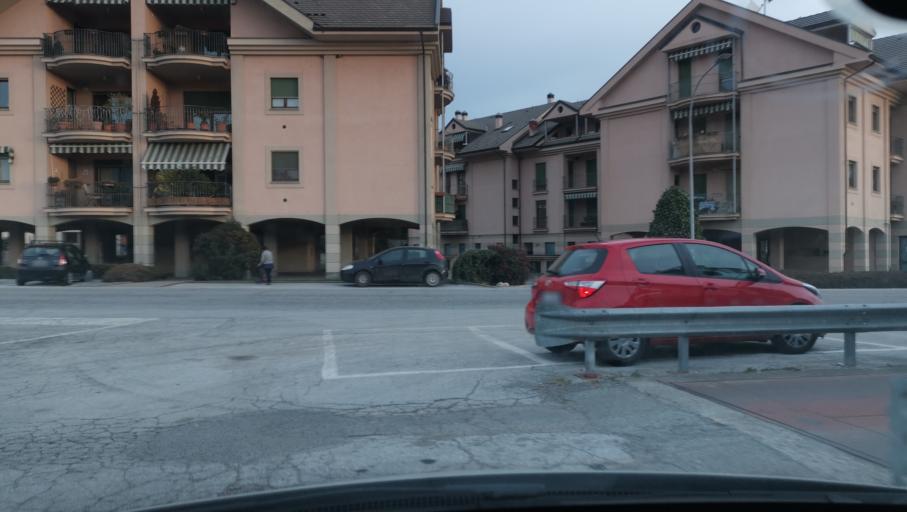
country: IT
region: Piedmont
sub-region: Provincia di Cuneo
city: Caraglio
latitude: 44.4140
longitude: 7.4360
